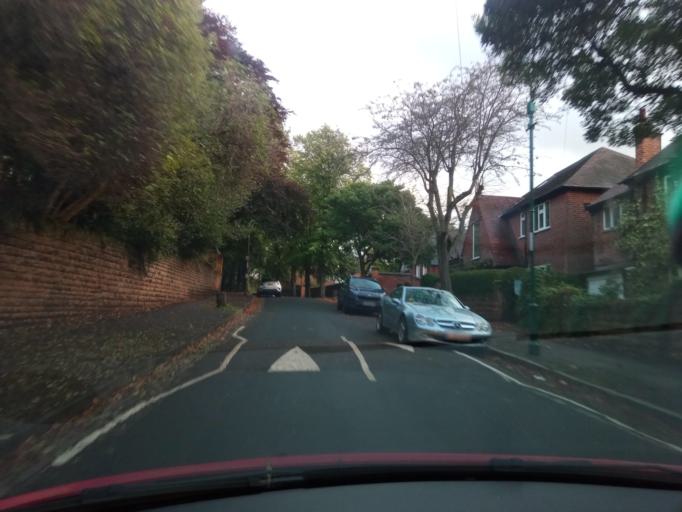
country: GB
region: England
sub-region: Nottingham
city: Nottingham
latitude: 52.9715
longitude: -1.1473
